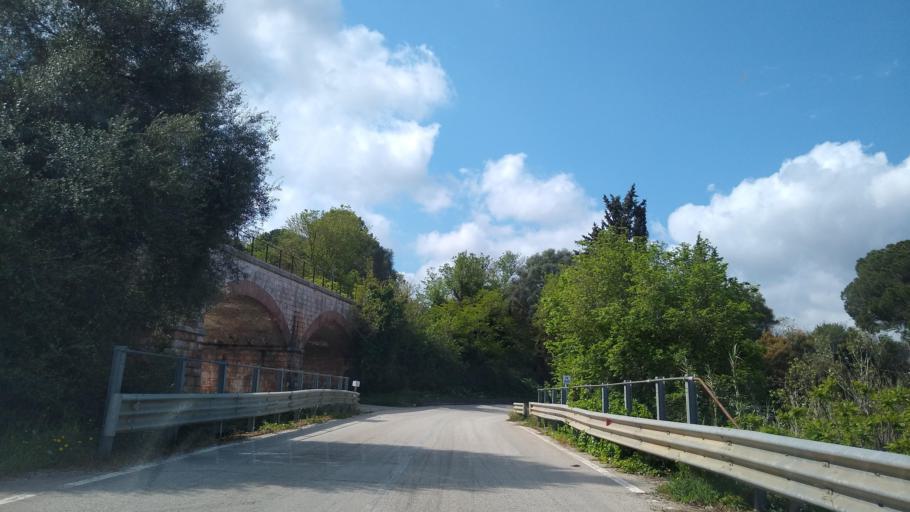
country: IT
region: Sicily
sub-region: Trapani
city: Calatafimi
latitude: 37.9452
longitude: 12.8610
